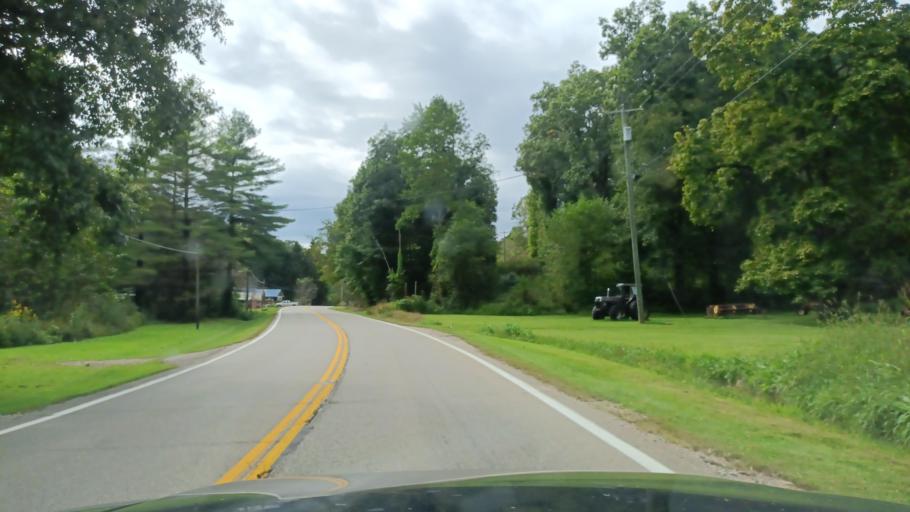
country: US
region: Ohio
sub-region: Vinton County
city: McArthur
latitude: 39.2716
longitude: -82.5654
